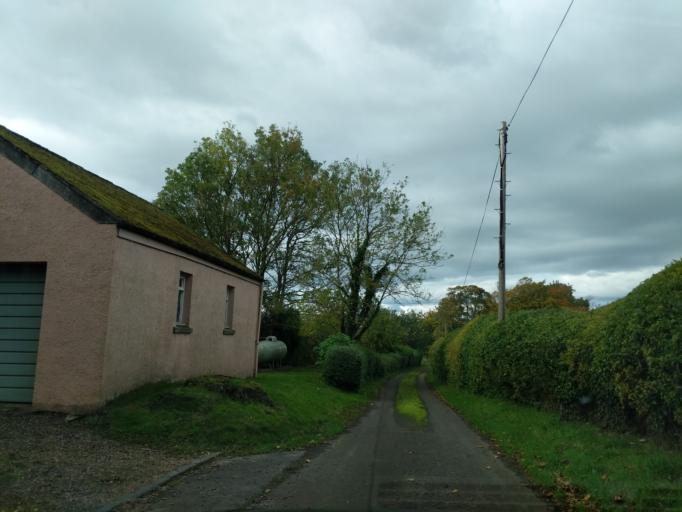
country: GB
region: Scotland
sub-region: East Lothian
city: East Linton
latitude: 55.9422
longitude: -2.7126
